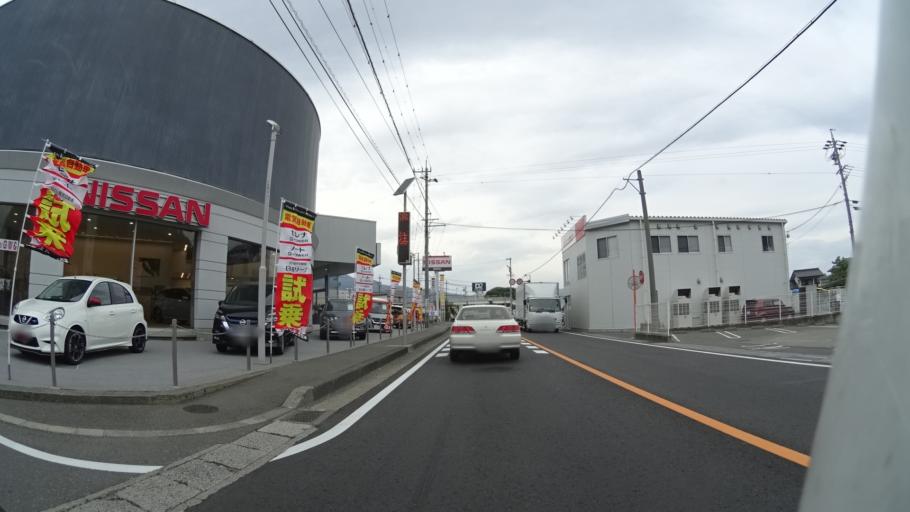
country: JP
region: Nagano
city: Nagano-shi
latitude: 36.5237
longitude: 138.1255
